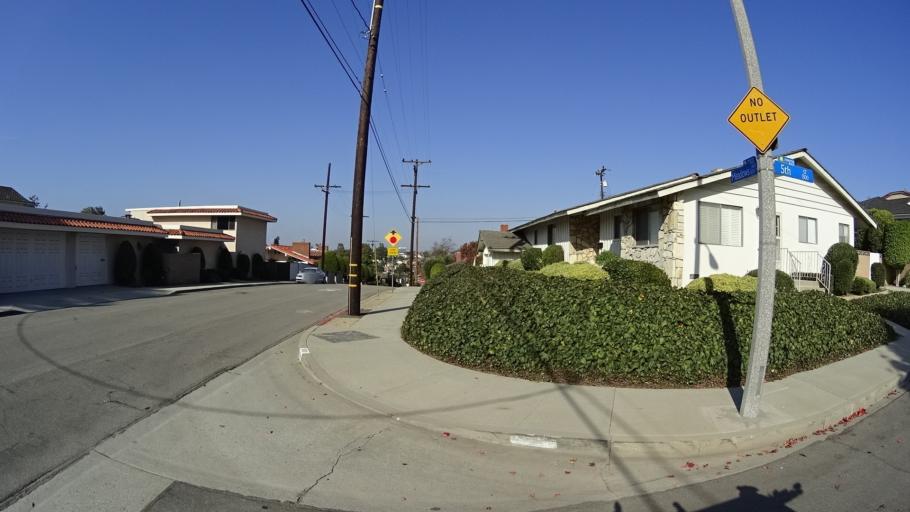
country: US
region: California
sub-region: Los Angeles County
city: Manhattan Beach
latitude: 33.8819
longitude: -118.3916
